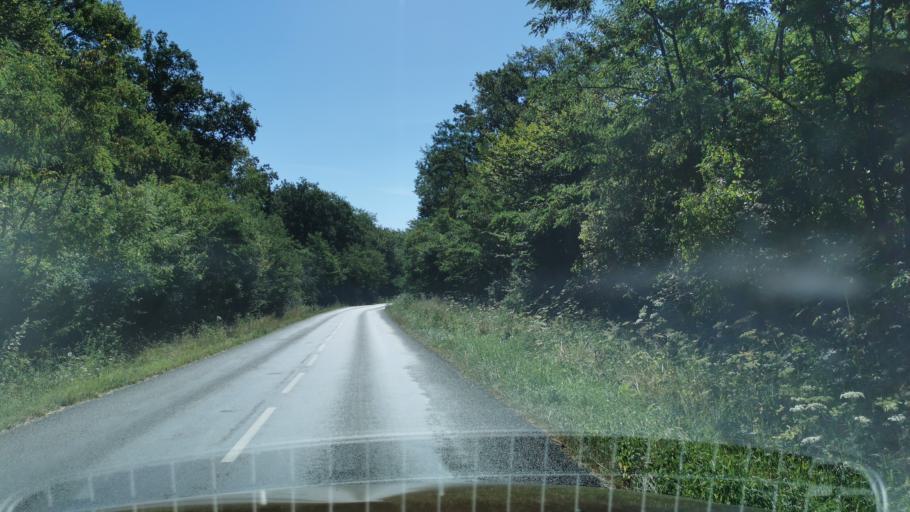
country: FR
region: Bourgogne
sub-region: Departement de Saone-et-Loire
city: Montchanin
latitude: 46.7627
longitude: 4.4732
